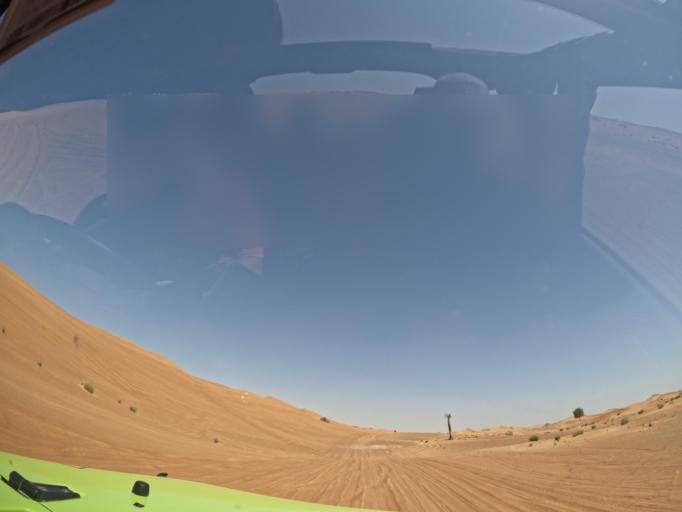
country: AE
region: Ash Shariqah
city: Adh Dhayd
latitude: 24.9938
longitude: 55.7246
